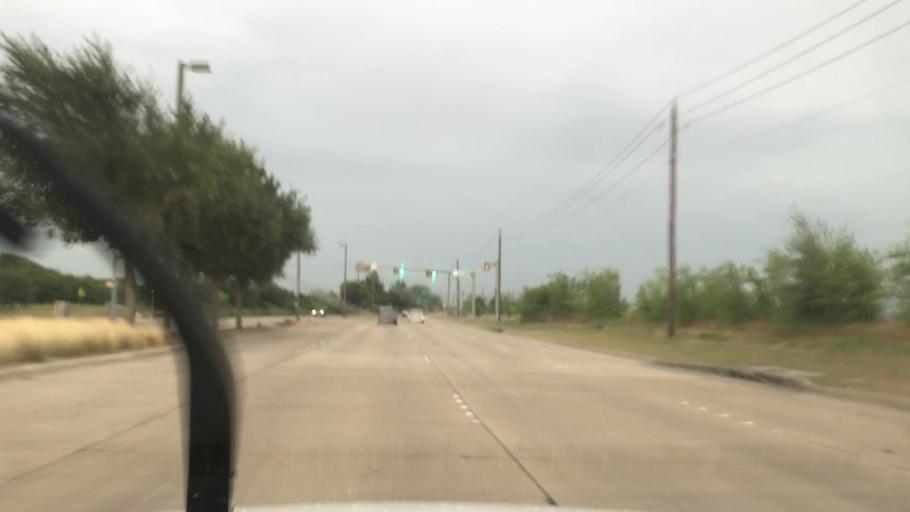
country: US
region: Texas
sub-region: Dallas County
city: Mesquite
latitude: 32.7373
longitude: -96.5669
